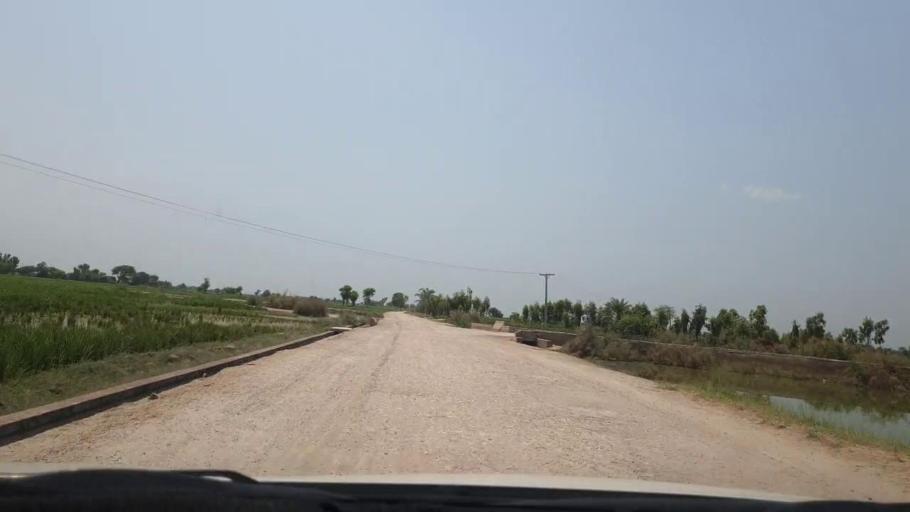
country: PK
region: Sindh
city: Radhan
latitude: 27.2429
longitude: 68.0010
